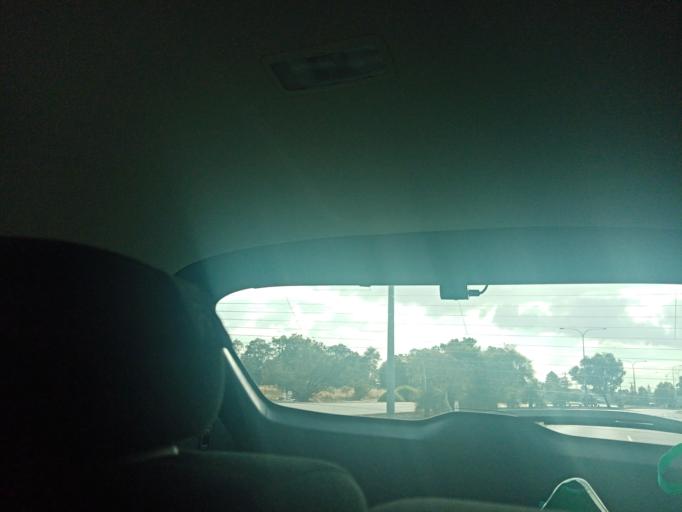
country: AU
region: Western Australia
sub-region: City of Cockburn
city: South Lake
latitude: -32.1251
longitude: 115.8370
